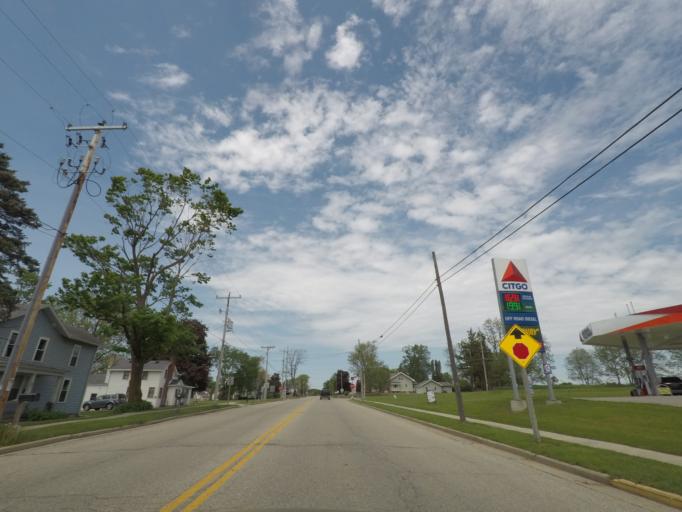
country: US
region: Wisconsin
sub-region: Rock County
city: Orfordville
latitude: 42.6320
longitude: -89.2626
